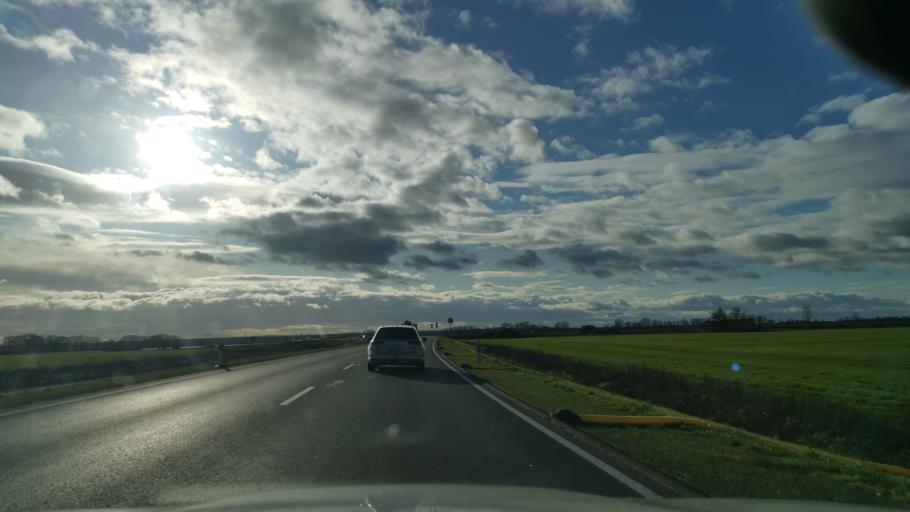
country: DE
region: Saxony-Anhalt
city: Kemberg
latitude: 51.8164
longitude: 12.6447
